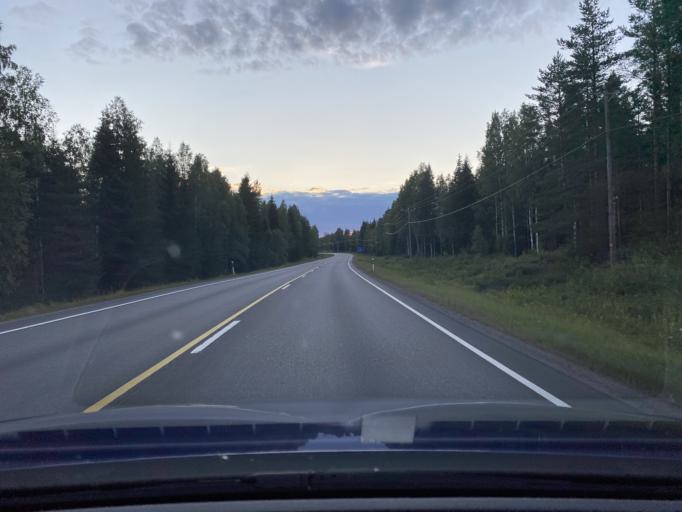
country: FI
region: Uusimaa
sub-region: Helsinki
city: Kaerkoelae
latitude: 60.8238
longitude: 24.0260
